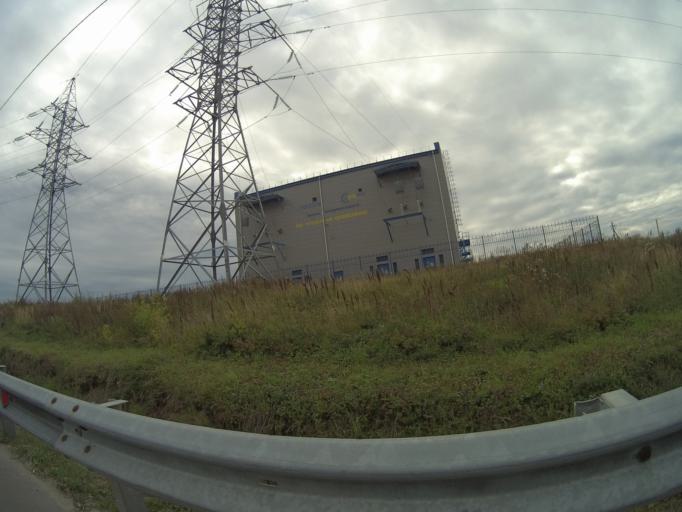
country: RU
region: Vladimir
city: Vladimir
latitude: 56.1203
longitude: 40.3413
